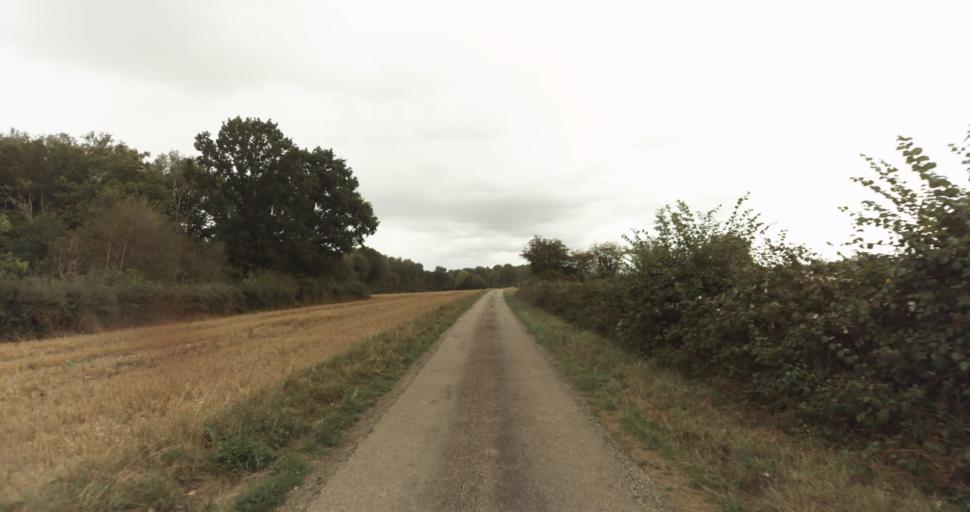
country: FR
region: Lower Normandy
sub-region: Departement du Calvados
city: Orbec
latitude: 48.9105
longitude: 0.3557
